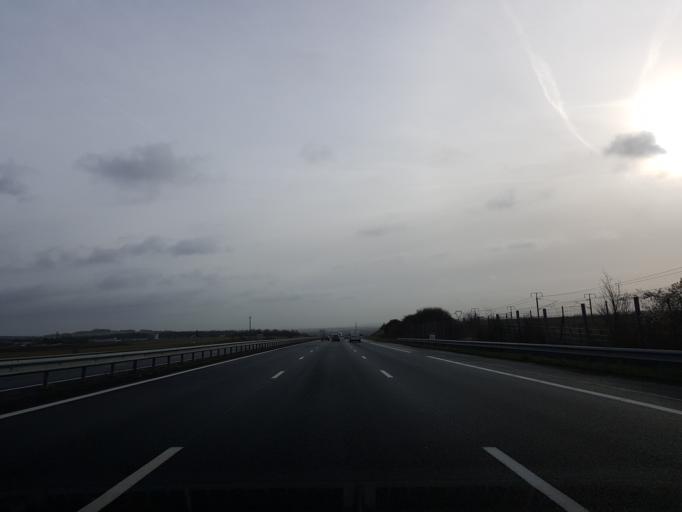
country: FR
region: Ile-de-France
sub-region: Departement de Seine-et-Marne
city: Montereau-Fault-Yonne
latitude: 48.4099
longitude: 2.9590
